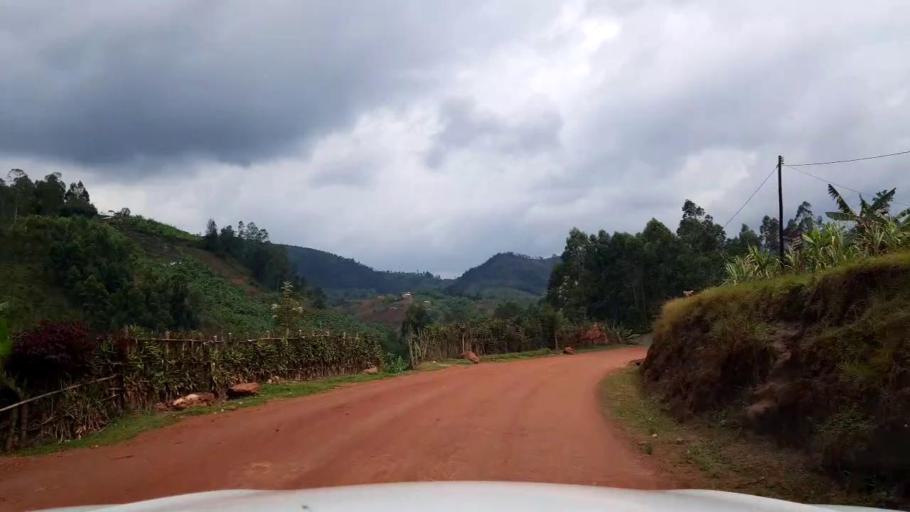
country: RW
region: Northern Province
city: Musanze
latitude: -1.6586
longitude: 29.7997
